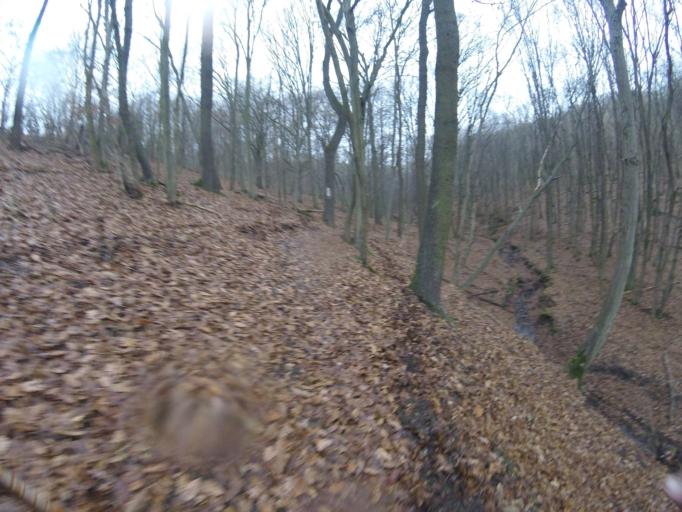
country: HU
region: Pest
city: Szob
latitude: 47.8787
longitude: 18.8480
